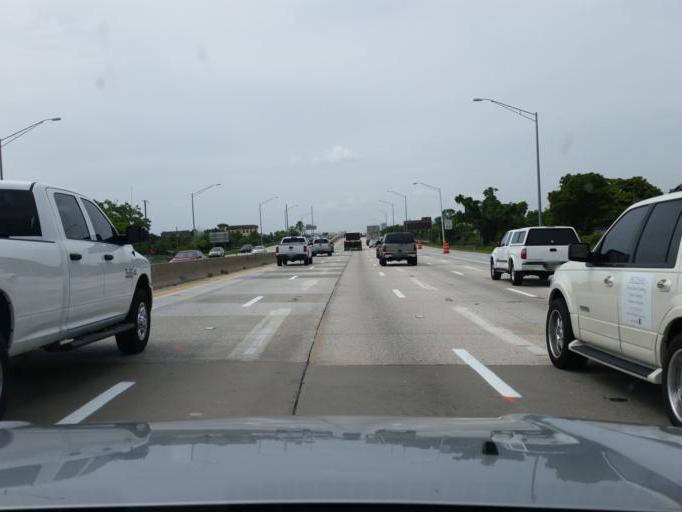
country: US
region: Florida
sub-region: Orange County
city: Fairview Shores
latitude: 28.5854
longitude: -81.3753
